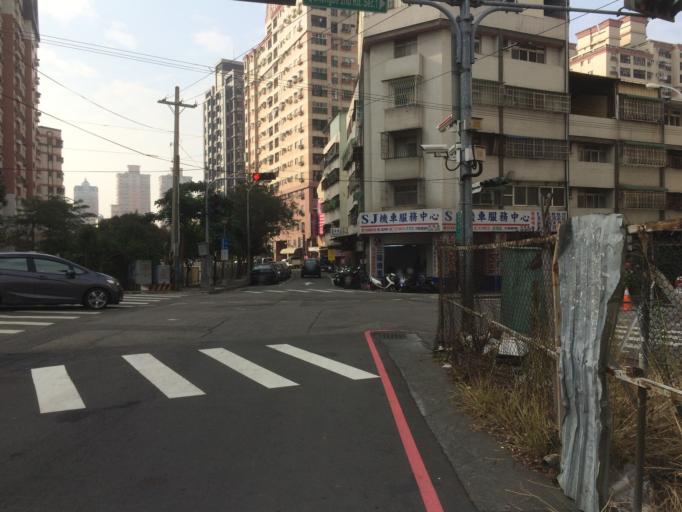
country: TW
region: Taiwan
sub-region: Taichung City
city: Taichung
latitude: 24.1767
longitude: 120.6936
